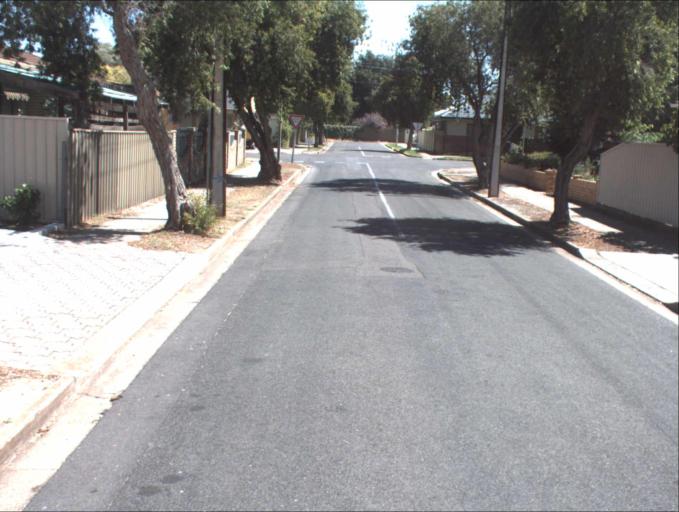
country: AU
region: South Australia
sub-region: Port Adelaide Enfield
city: Klemzig
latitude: -34.8759
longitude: 138.6359
